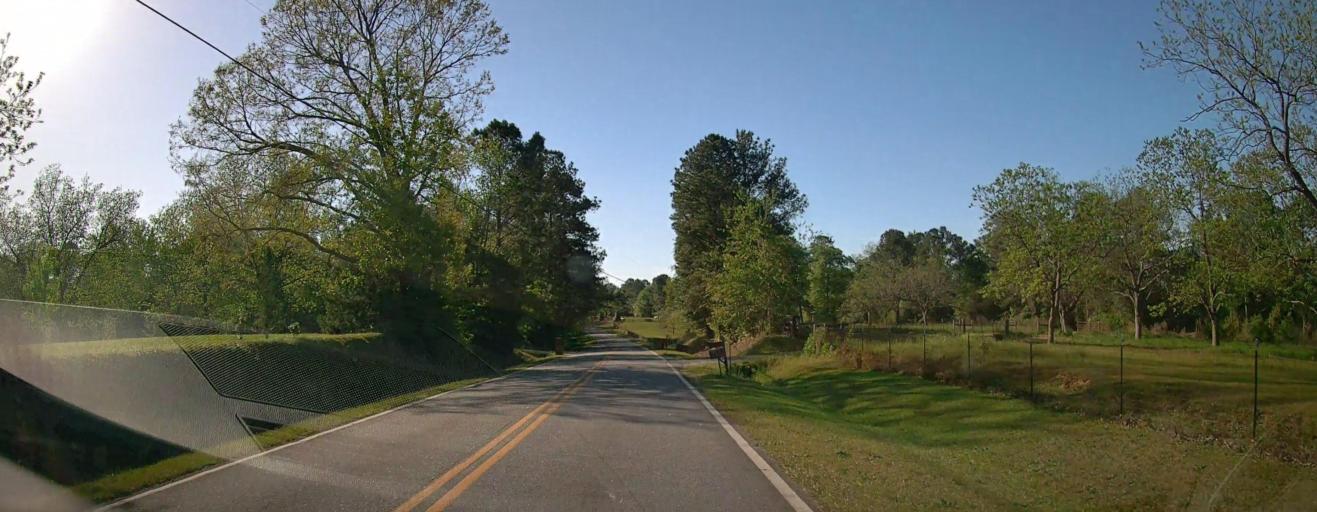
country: US
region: Georgia
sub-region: Houston County
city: Perry
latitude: 32.4784
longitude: -83.7949
